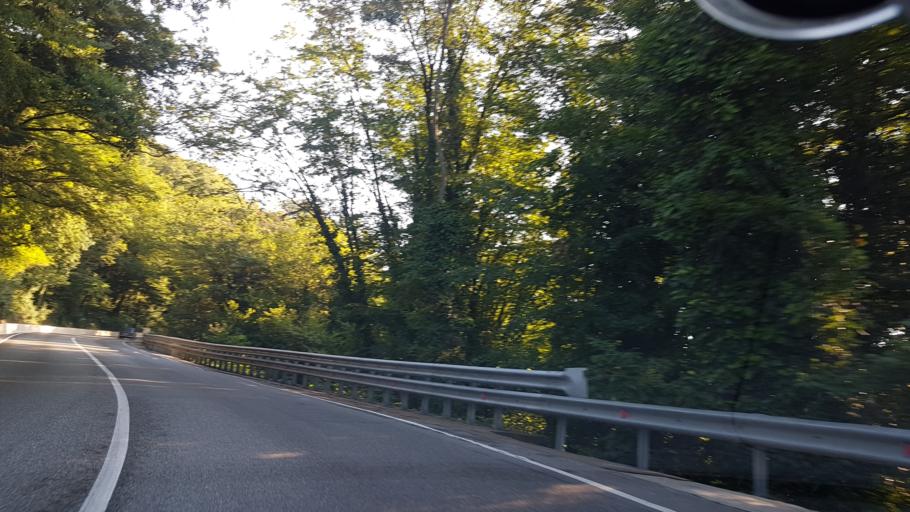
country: RU
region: Krasnodarskiy
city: Gornoye Loo
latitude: 43.6697
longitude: 39.6170
